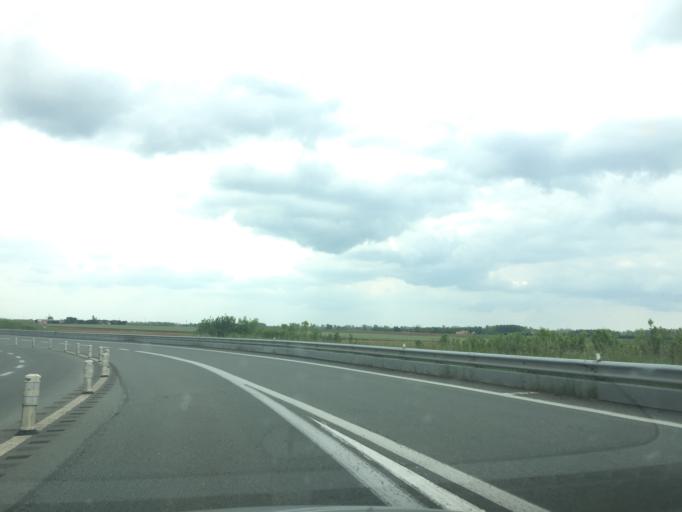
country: FR
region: Pays de la Loire
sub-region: Departement de la Vendee
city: Benet
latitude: 46.3892
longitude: -0.6567
